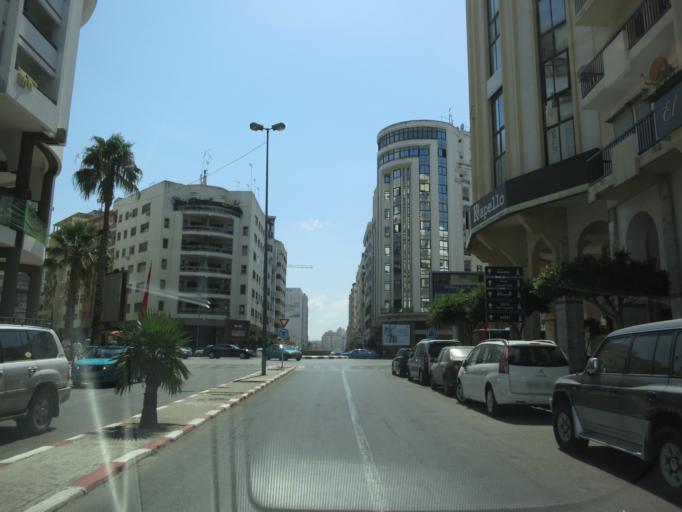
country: MA
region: Tanger-Tetouan
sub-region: Tanger-Assilah
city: Tangier
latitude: 35.7760
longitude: -5.8001
